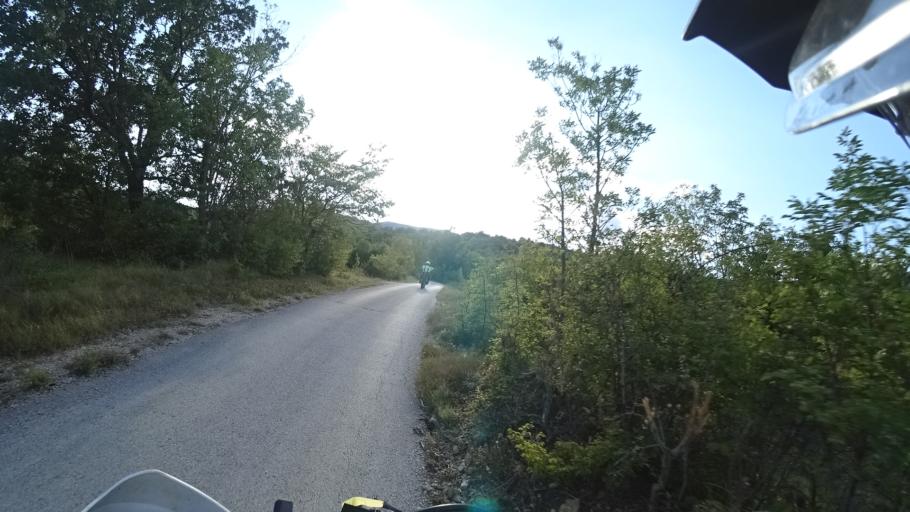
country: HR
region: Sibensko-Kniniska
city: Knin
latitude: 44.2031
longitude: 16.0690
